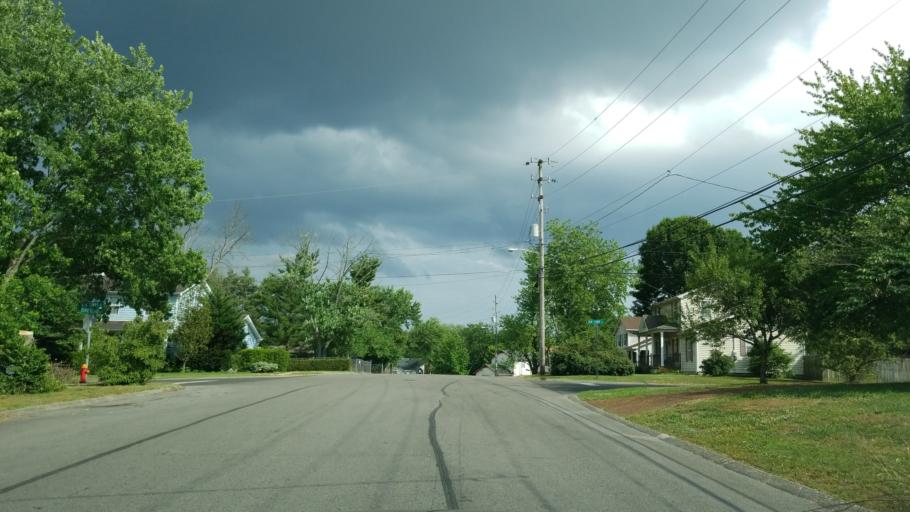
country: US
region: Tennessee
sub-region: Rutherford County
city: La Vergne
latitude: 36.0707
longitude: -86.6059
